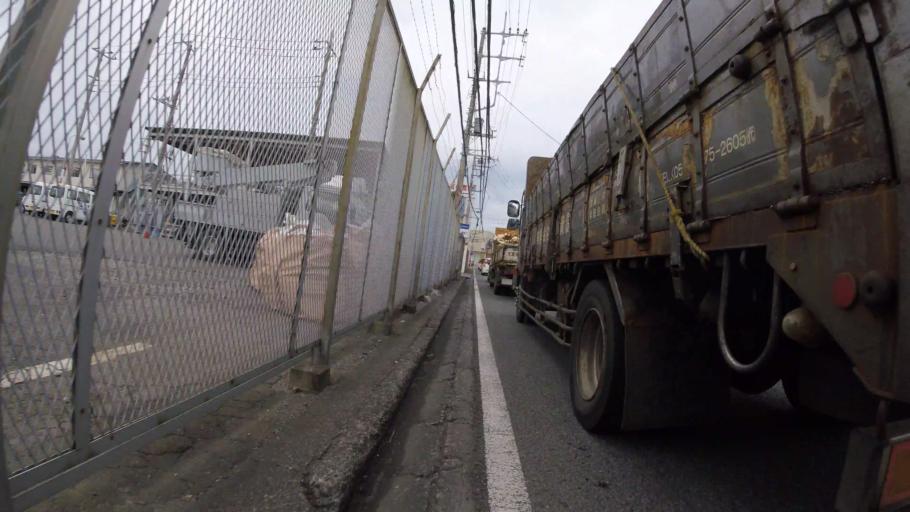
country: JP
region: Shizuoka
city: Numazu
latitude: 35.1079
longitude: 138.8914
